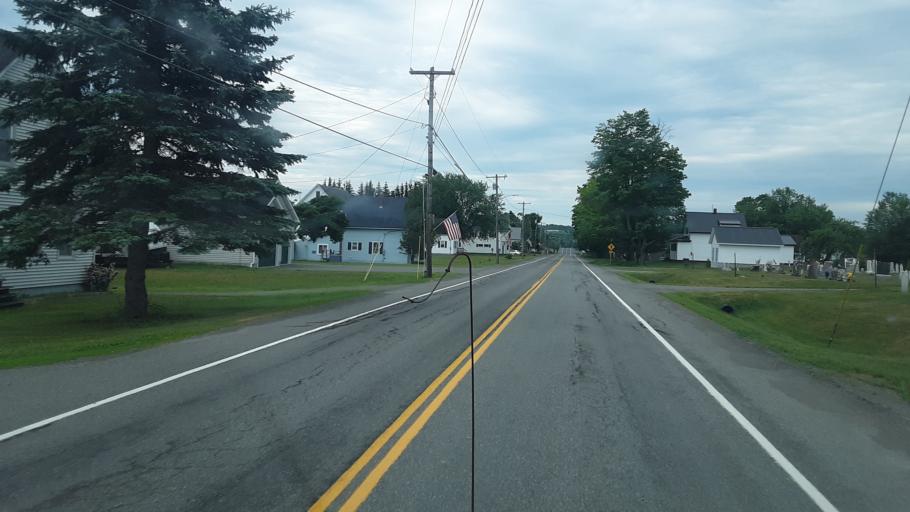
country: US
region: Maine
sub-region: Penobscot County
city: Patten
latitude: 46.0052
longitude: -68.4467
